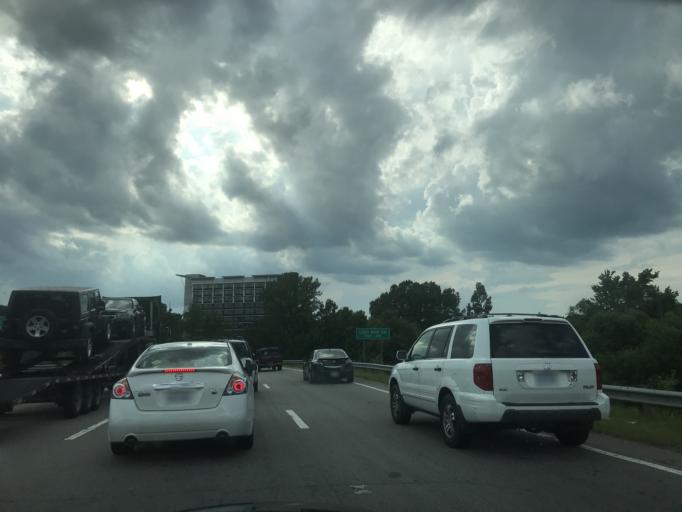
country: US
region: North Carolina
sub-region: Wake County
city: West Raleigh
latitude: 35.8367
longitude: -78.6683
